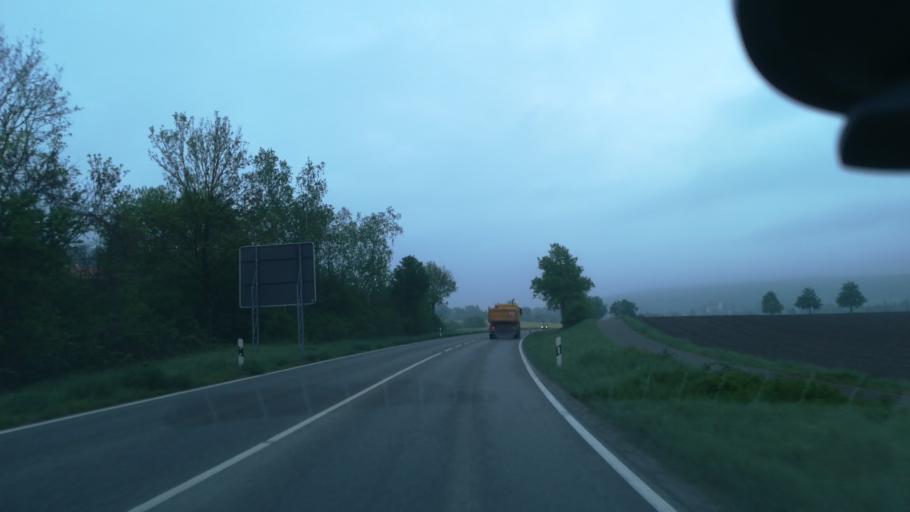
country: DE
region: Baden-Wuerttemberg
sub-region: Freiburg Region
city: Steisslingen
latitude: 47.7846
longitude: 8.9159
